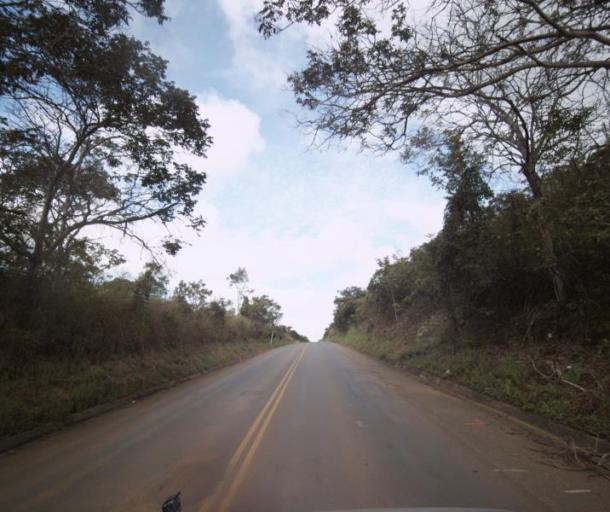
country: BR
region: Goias
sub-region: Pirenopolis
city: Pirenopolis
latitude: -15.8566
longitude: -48.7670
